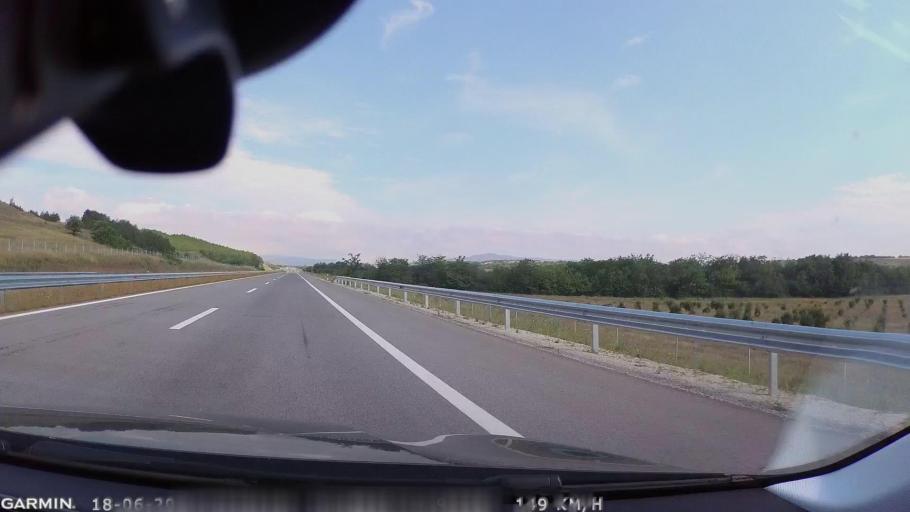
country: MK
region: Sveti Nikole
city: Sveti Nikole
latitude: 41.8960
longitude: 21.9217
